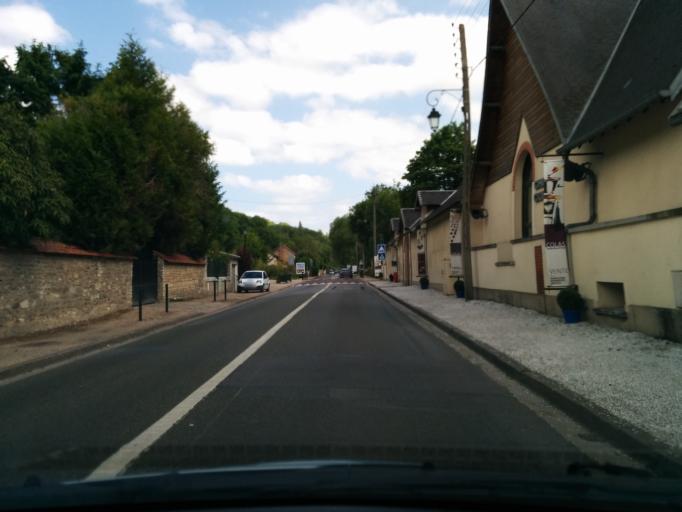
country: FR
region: Ile-de-France
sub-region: Departement des Yvelines
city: Maule
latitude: 48.9082
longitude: 1.8580
